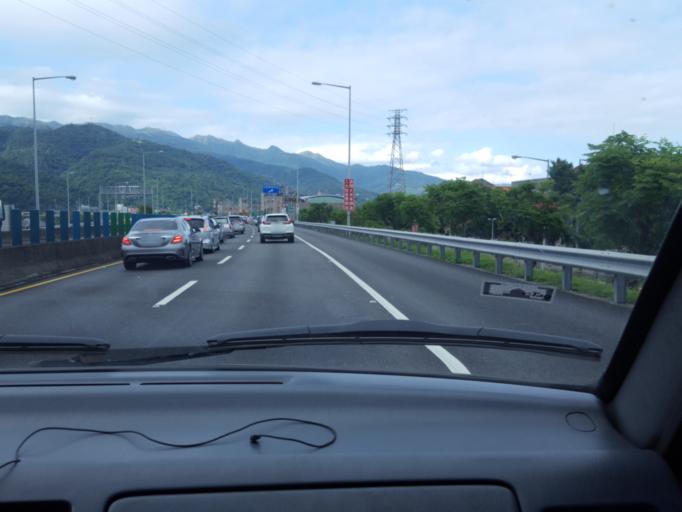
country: TW
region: Taiwan
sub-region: Yilan
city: Yilan
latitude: 24.8297
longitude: 121.7905
